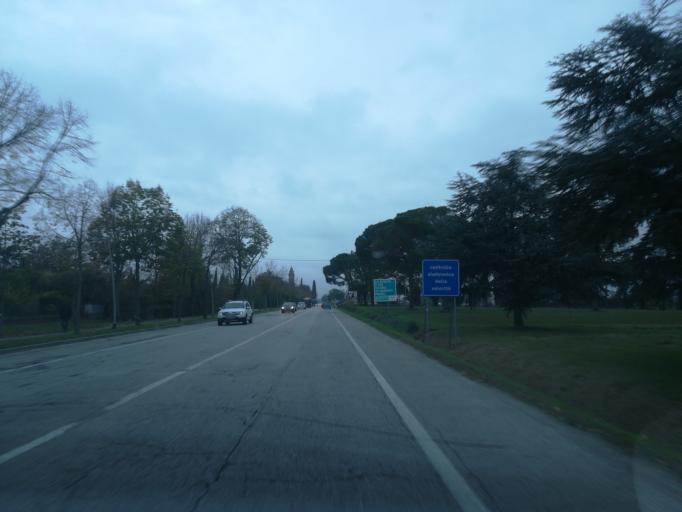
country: IT
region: Emilia-Romagna
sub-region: Provincia di Bologna
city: Toscanella
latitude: 44.3685
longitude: 11.6757
